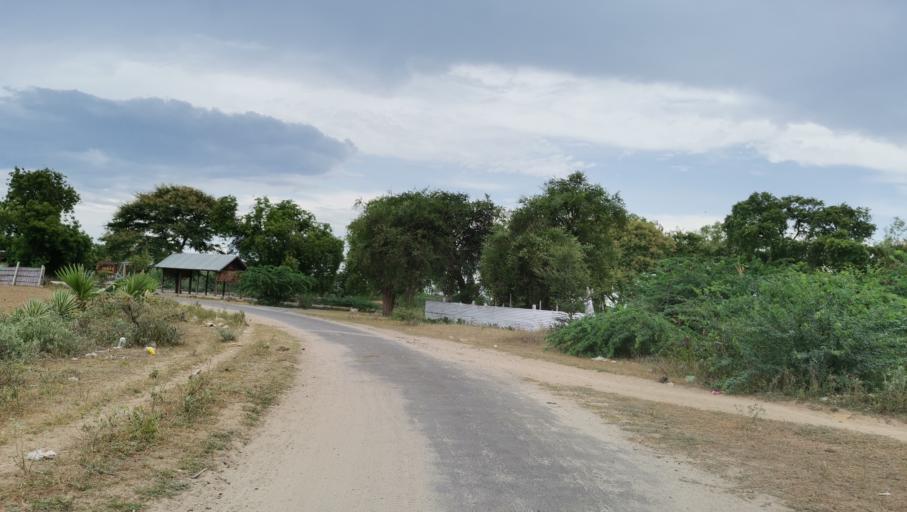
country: MM
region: Mandalay
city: Myingyan
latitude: 21.8147
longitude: 95.3964
